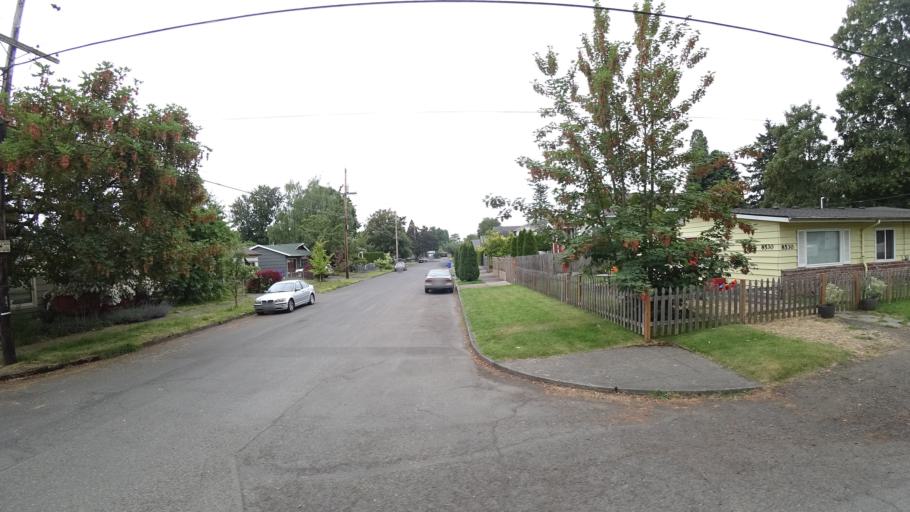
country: US
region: Oregon
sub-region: Multnomah County
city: Lents
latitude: 45.5122
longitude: -122.5752
